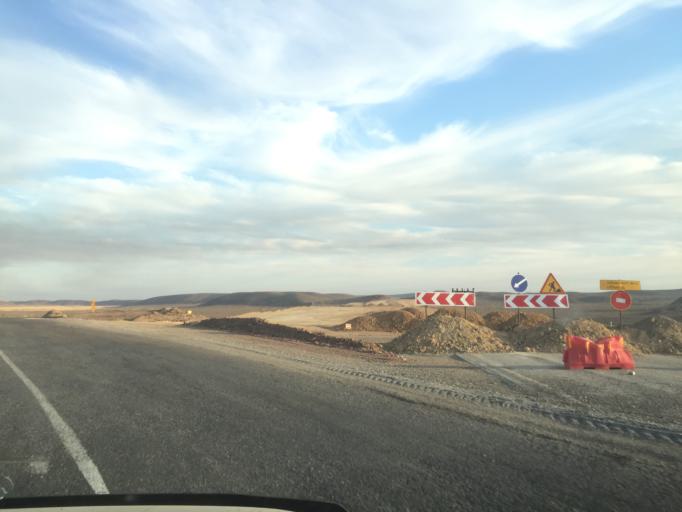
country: KZ
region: Almaty Oblysy
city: Ulken
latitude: 45.0681
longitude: 73.9949
